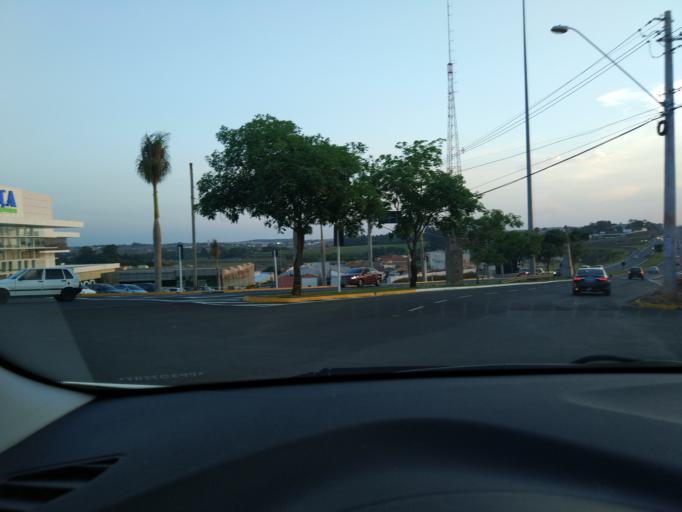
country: BR
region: Sao Paulo
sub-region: Botucatu
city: Botucatu
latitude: -22.9003
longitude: -48.4496
